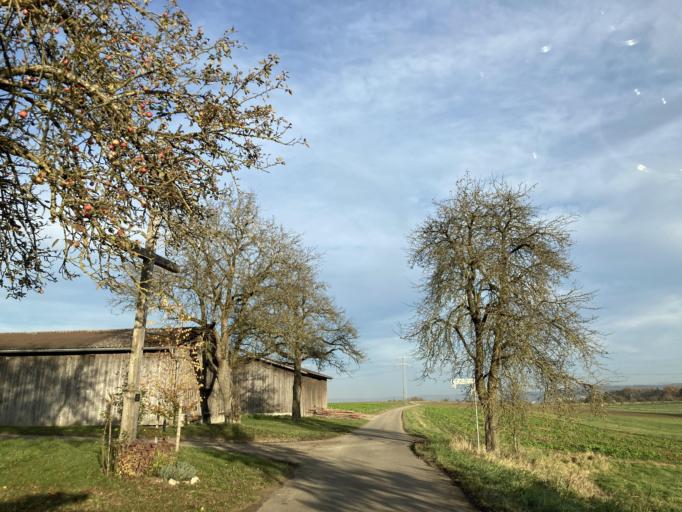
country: DE
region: Baden-Wuerttemberg
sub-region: Tuebingen Region
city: Rottenburg
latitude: 48.4678
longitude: 8.8871
